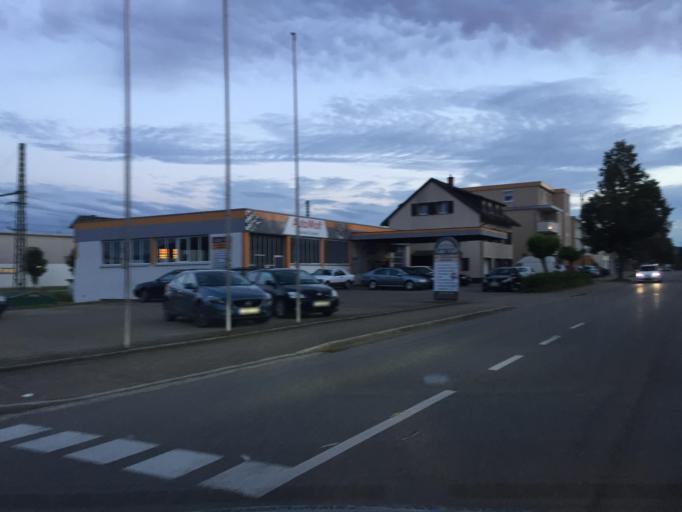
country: CH
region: Schaffhausen
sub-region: Bezirk Unterklettgau
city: Wilchingen
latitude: 47.6588
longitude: 8.4285
